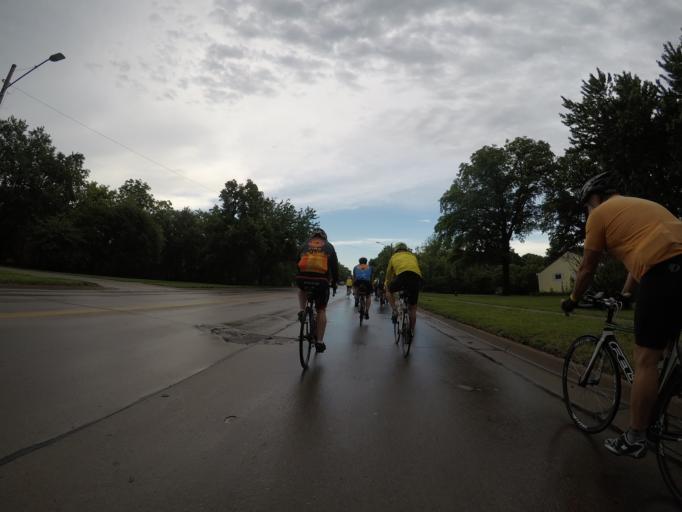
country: US
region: Kansas
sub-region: Shawnee County
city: Topeka
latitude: 39.0251
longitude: -95.6969
